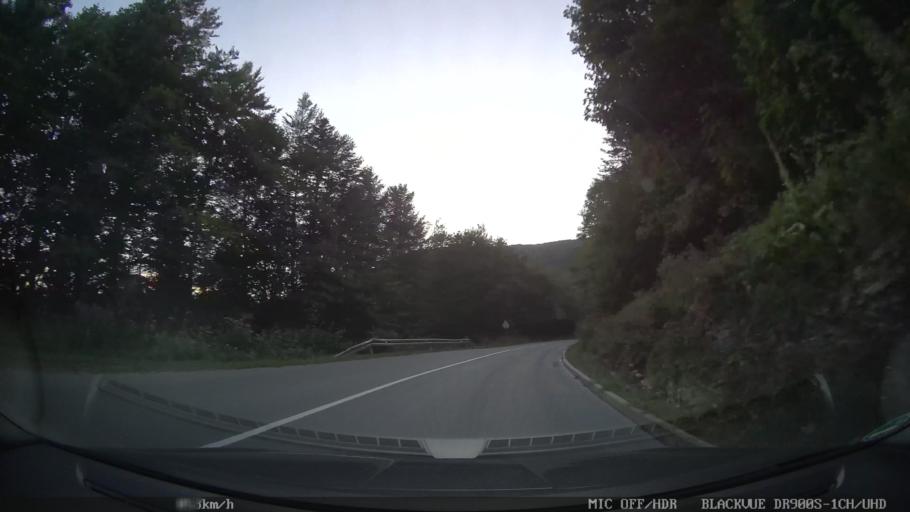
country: HR
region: Primorsko-Goranska
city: Novi Vinodolski
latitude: 45.1700
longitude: 14.9694
